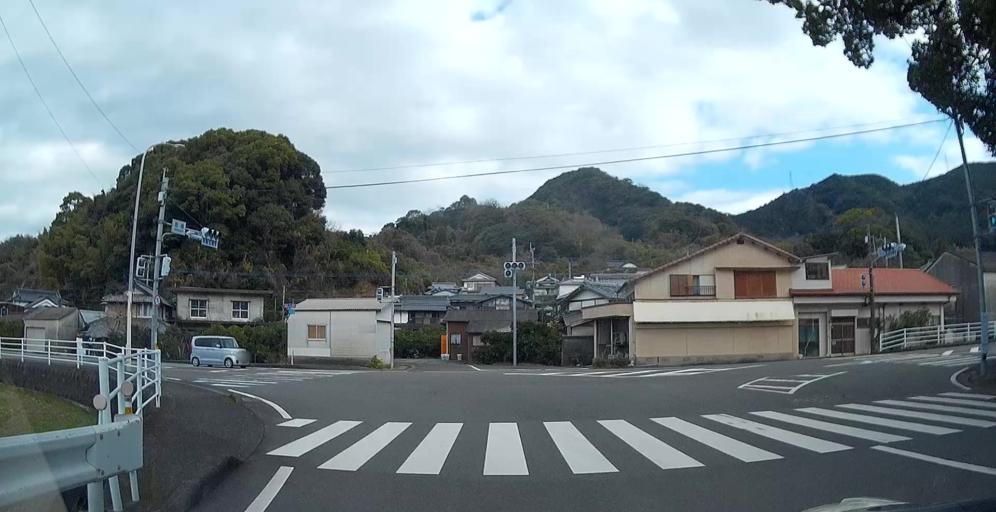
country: JP
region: Kumamoto
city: Minamata
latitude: 32.3301
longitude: 130.4856
